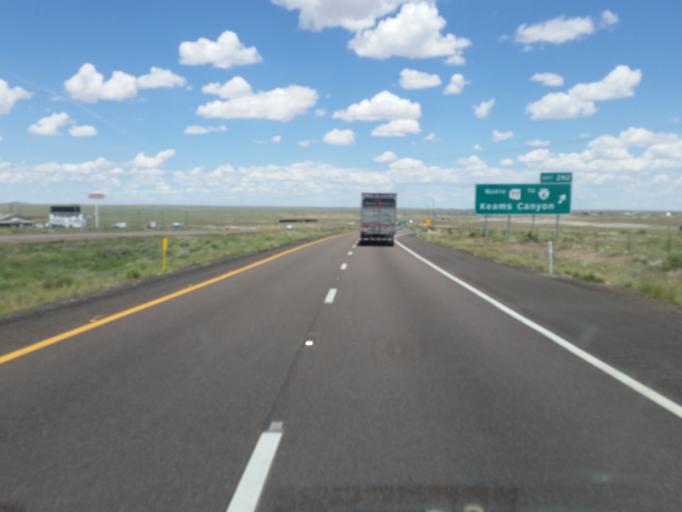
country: US
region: Arizona
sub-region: Navajo County
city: Holbrook
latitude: 34.9706
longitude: -110.0922
